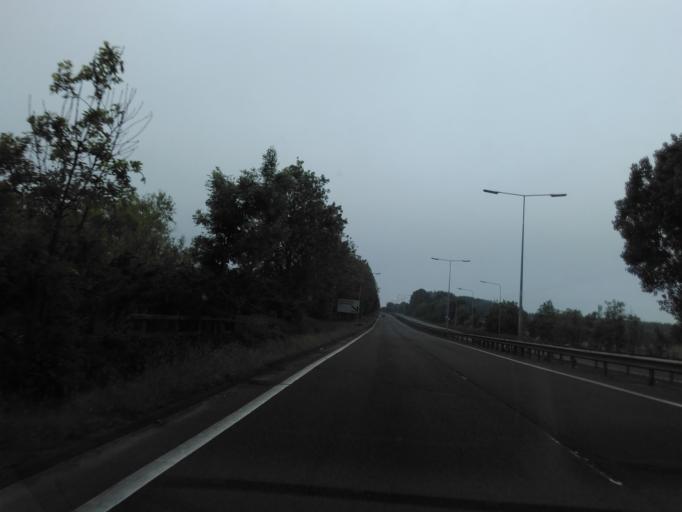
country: GB
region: England
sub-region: Kent
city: Dunkirk
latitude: 51.3126
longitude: 0.9483
